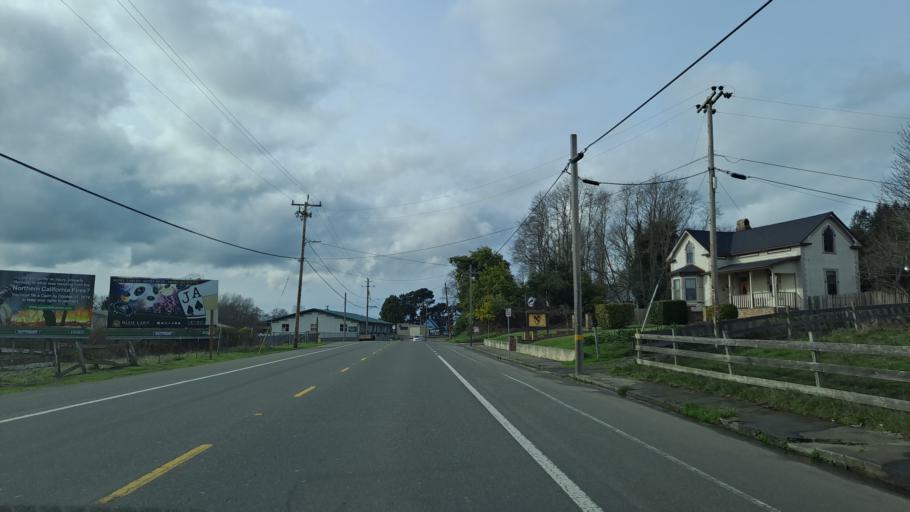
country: US
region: California
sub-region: Humboldt County
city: Fortuna
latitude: 40.5990
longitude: -124.1637
